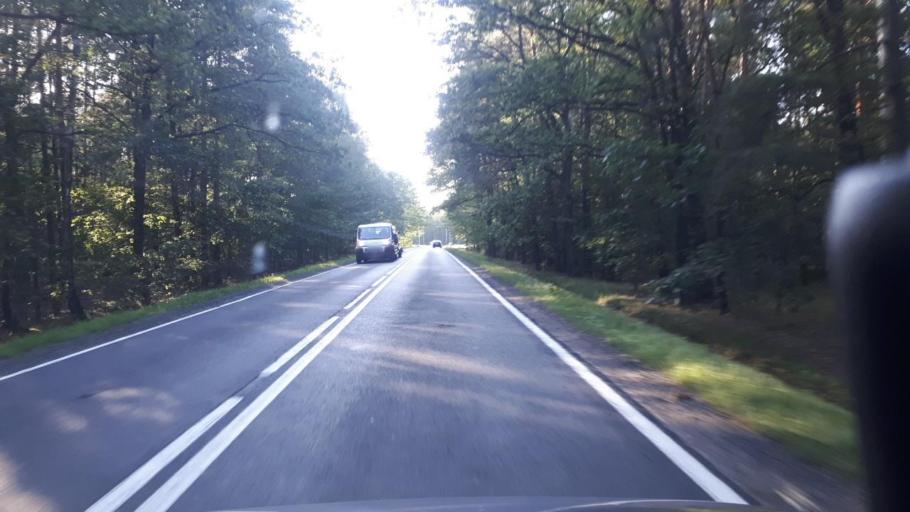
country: PL
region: Silesian Voivodeship
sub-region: Powiat lubliniecki
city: Sierakow Slaski
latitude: 50.8189
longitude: 18.5362
